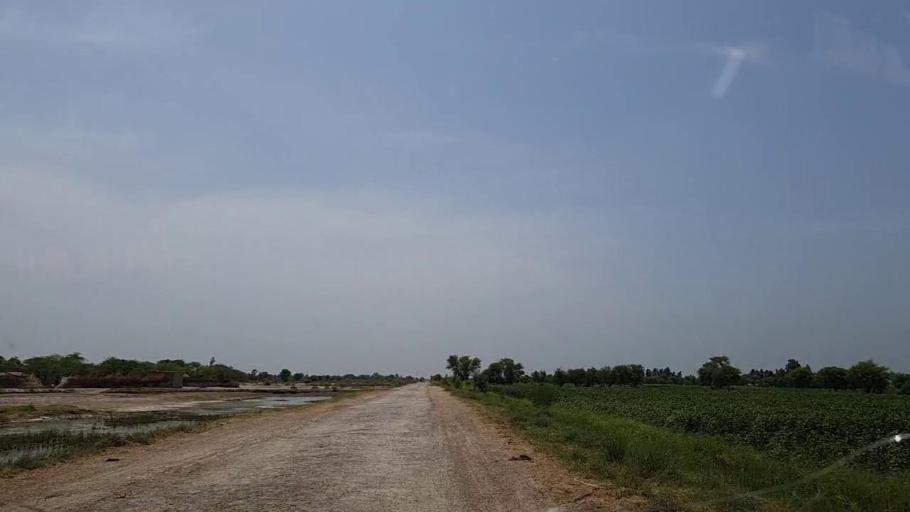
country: PK
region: Sindh
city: Khanpur
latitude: 27.8761
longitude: 69.4910
